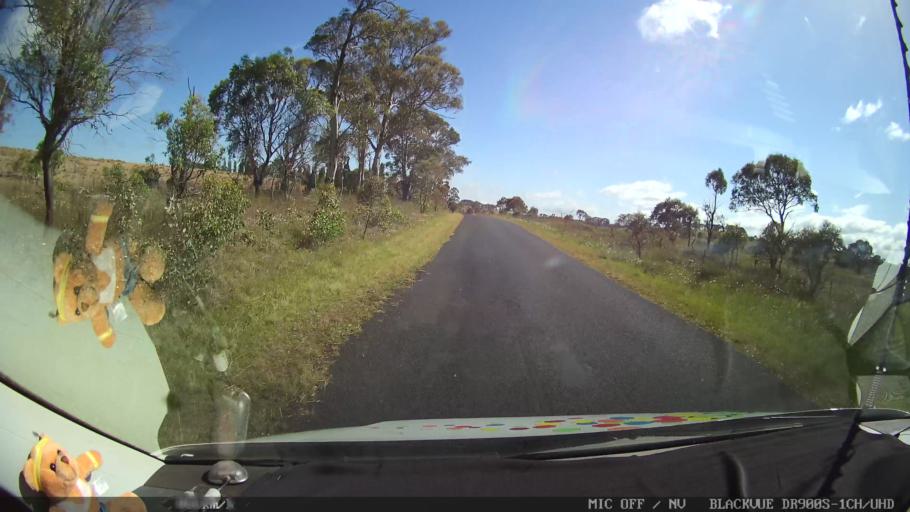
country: AU
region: New South Wales
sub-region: Guyra
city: Guyra
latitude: -30.1775
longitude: 151.6828
